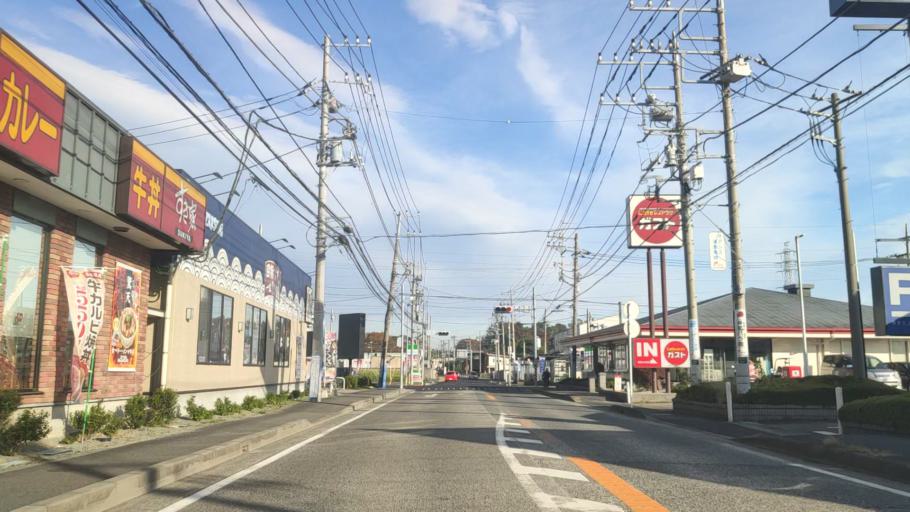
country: JP
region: Kanagawa
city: Atsugi
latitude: 35.4215
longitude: 139.3909
